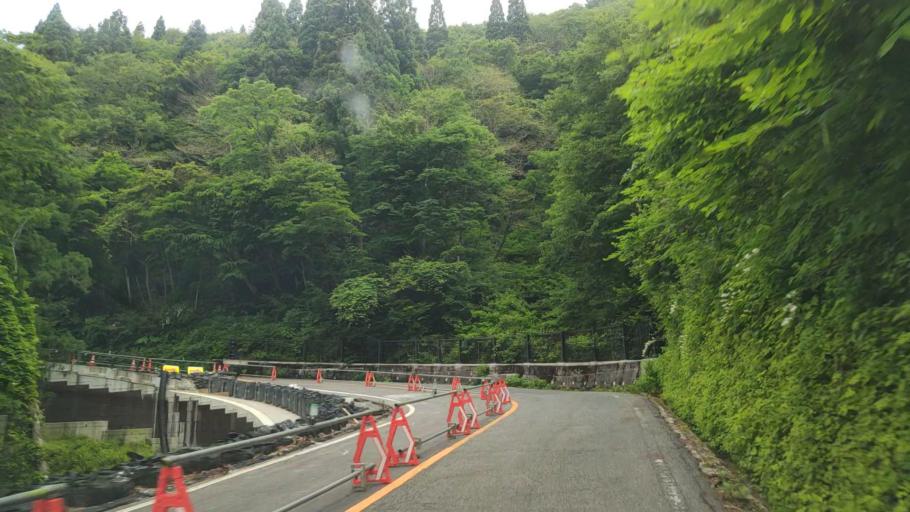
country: JP
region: Tottori
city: Yonago
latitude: 35.3490
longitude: 133.5487
